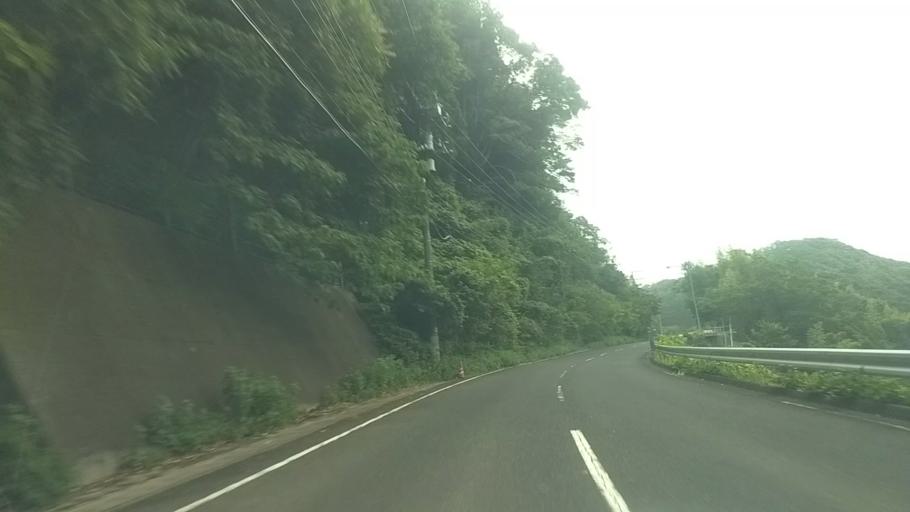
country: JP
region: Chiba
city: Katsuura
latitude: 35.2476
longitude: 140.2411
